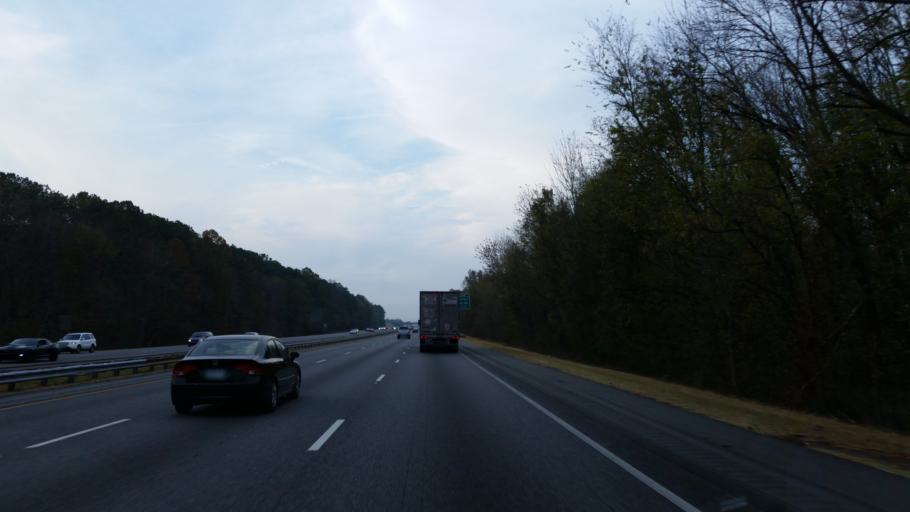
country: US
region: Georgia
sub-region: Bartow County
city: Cartersville
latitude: 34.2630
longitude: -84.8022
